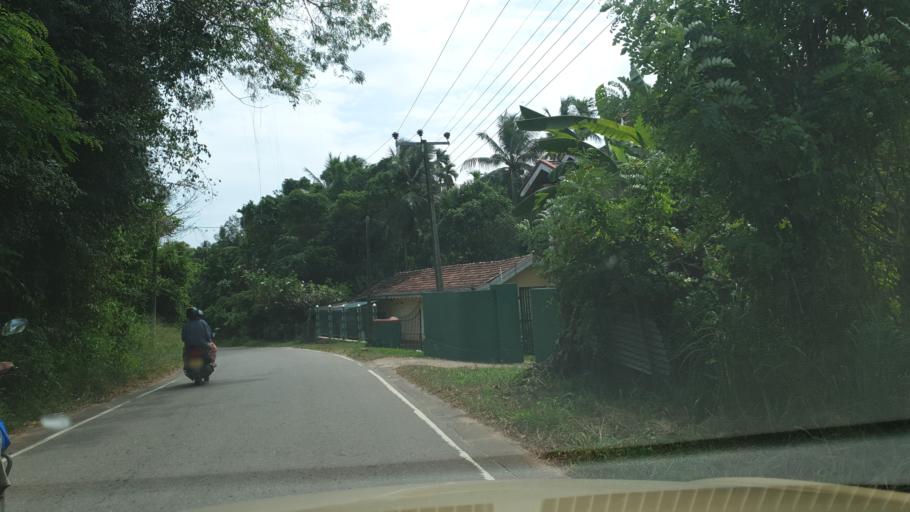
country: LK
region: North Western
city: Kuliyapitiya
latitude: 7.3469
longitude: 79.9851
